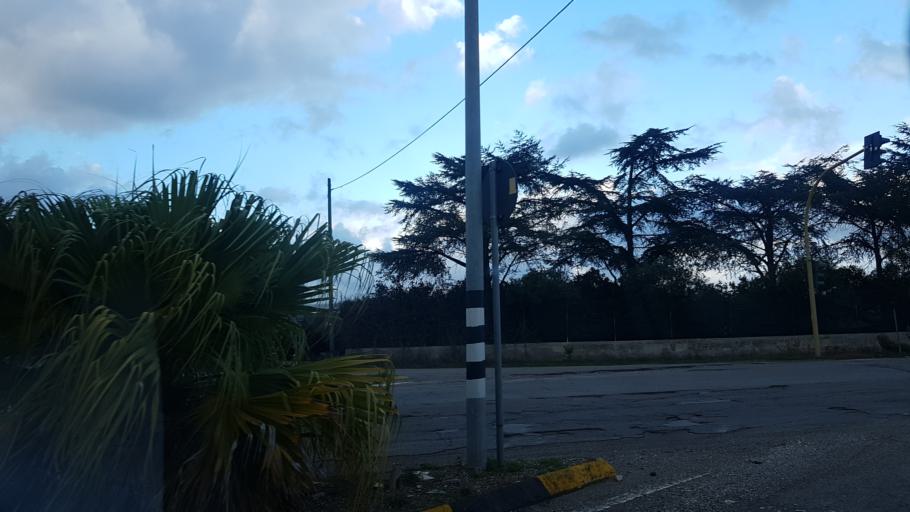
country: IT
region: Apulia
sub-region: Provincia di Brindisi
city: San Pietro Vernotico
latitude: 40.4992
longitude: 18.0040
